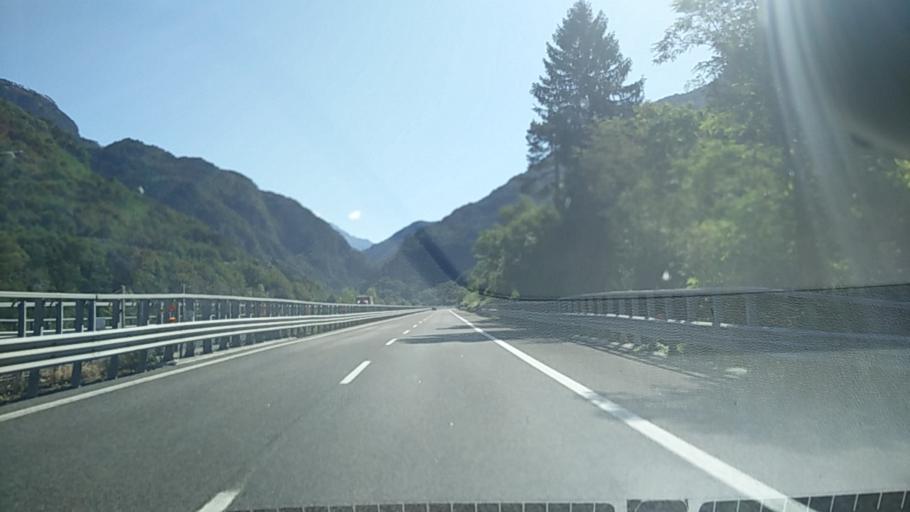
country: IT
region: Friuli Venezia Giulia
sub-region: Provincia di Udine
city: Resiutta
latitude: 46.3947
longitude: 13.2468
